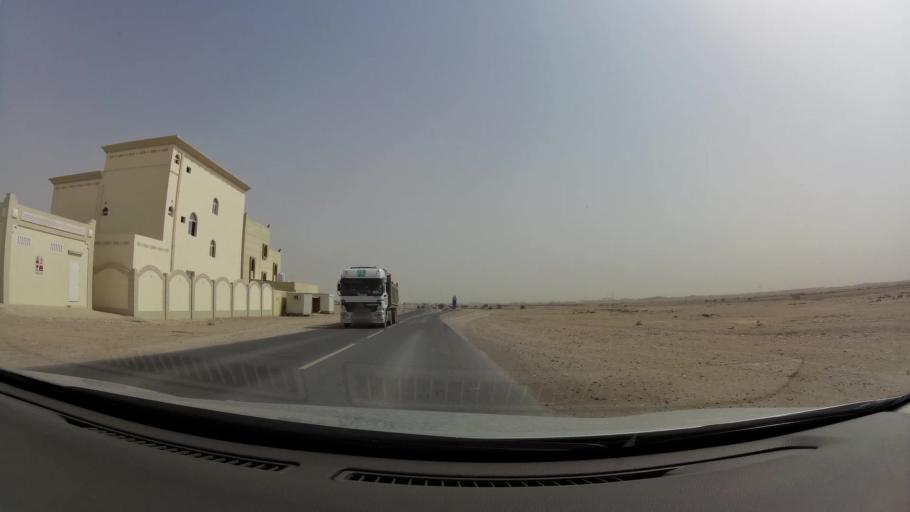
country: QA
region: Baladiyat ar Rayyan
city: Ar Rayyan
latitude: 25.2388
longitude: 51.3659
